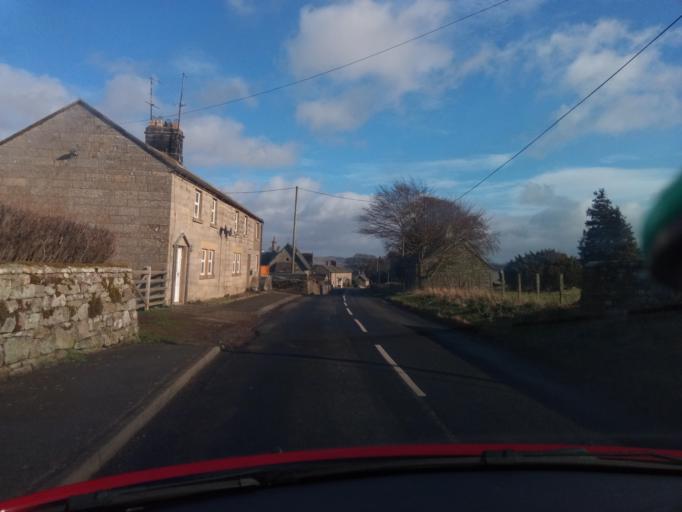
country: GB
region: England
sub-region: Northumberland
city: Rothbury
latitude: 55.2995
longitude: -2.0274
